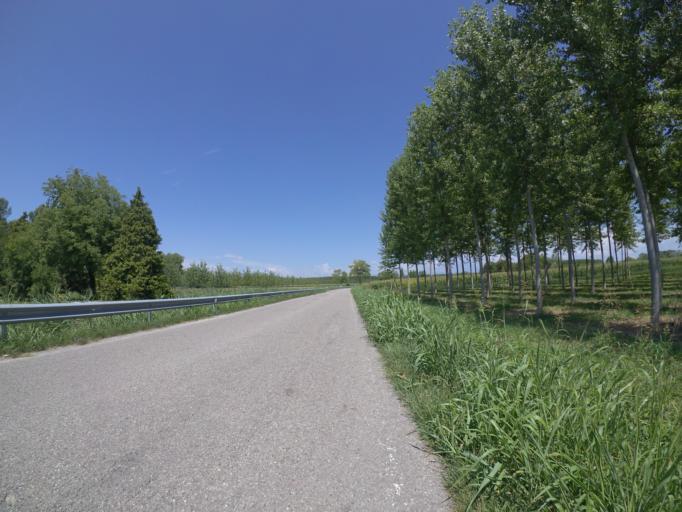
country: IT
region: Friuli Venezia Giulia
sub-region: Provincia di Udine
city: Talmassons
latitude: 45.8917
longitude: 13.1156
